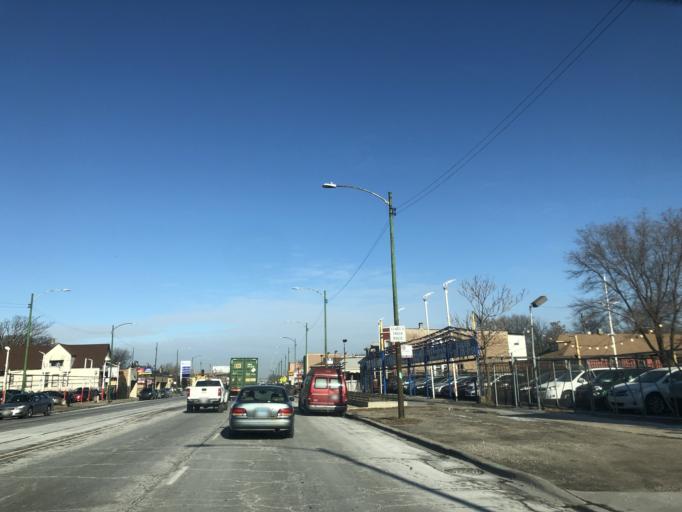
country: US
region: Illinois
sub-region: Cook County
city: Evergreen Park
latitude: 41.7611
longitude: -87.6831
